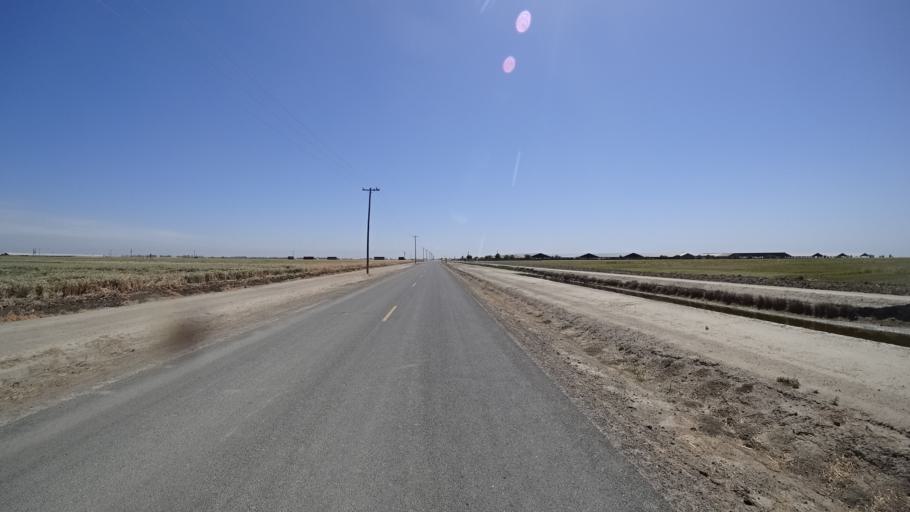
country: US
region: California
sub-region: Kings County
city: Armona
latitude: 36.1893
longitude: -119.6948
